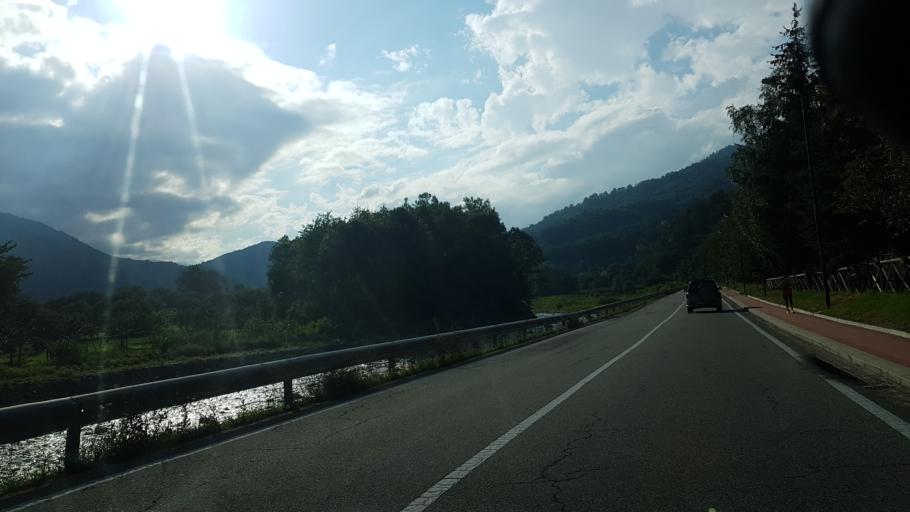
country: IT
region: Piedmont
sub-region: Provincia di Cuneo
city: Venasca
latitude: 44.5656
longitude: 7.3946
